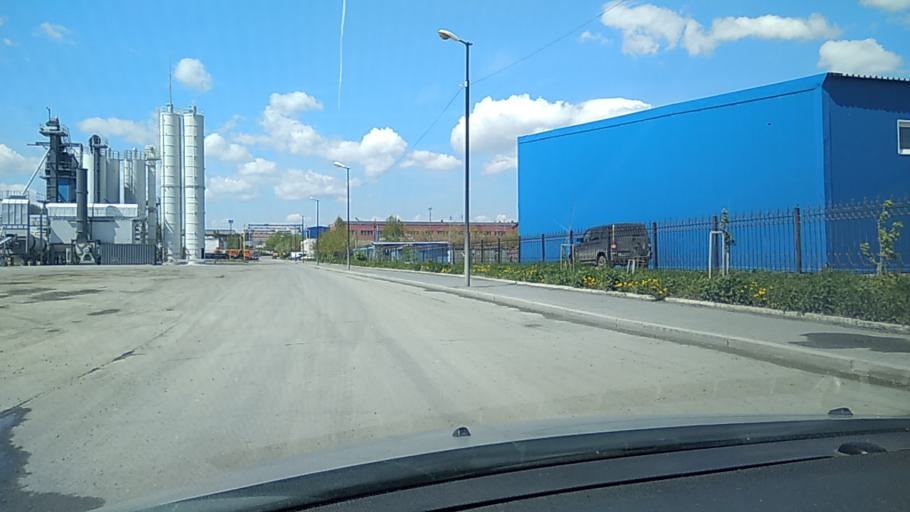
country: RU
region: Sverdlovsk
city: Istok
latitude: 56.7544
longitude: 60.7479
